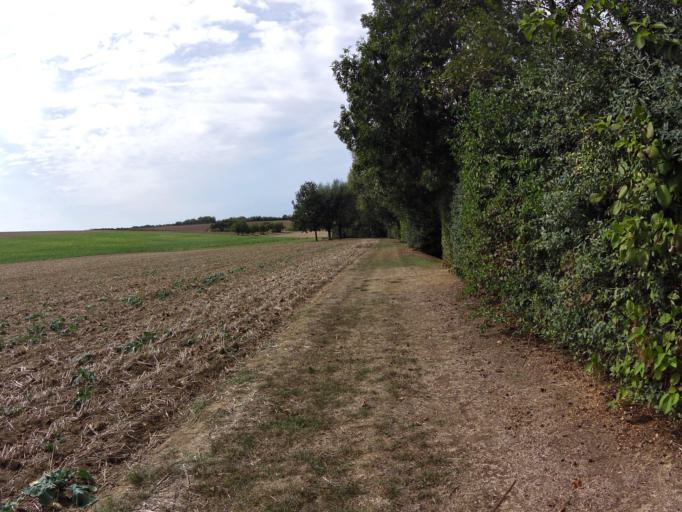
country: DE
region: Bavaria
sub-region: Regierungsbezirk Unterfranken
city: Waldbuttelbrunn
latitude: 49.7831
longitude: 9.8384
